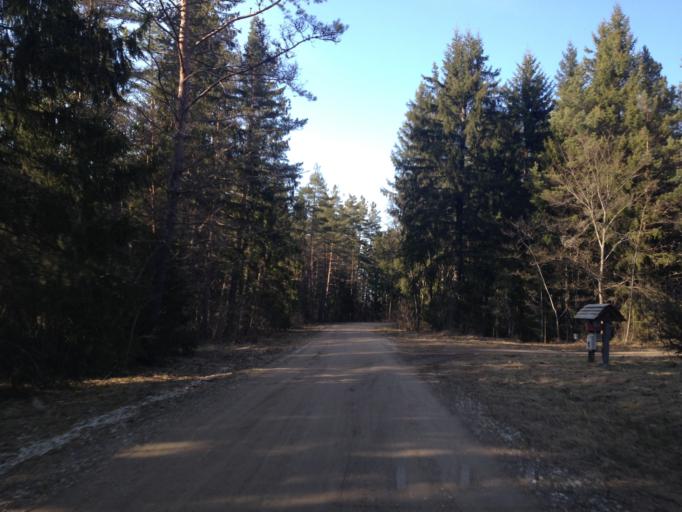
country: EE
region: Harju
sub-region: Nissi vald
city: Turba
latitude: 59.1096
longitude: 24.1573
